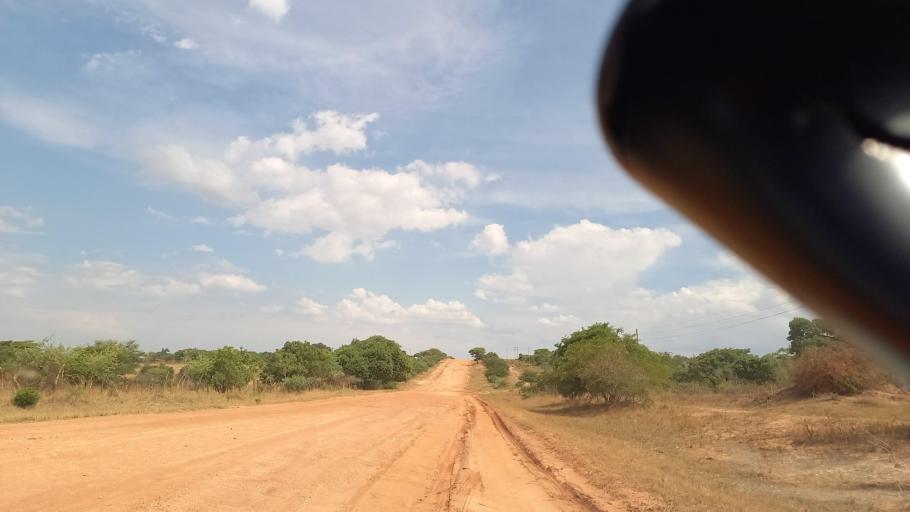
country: ZM
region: Lusaka
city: Kafue
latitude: -16.1270
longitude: 28.0447
